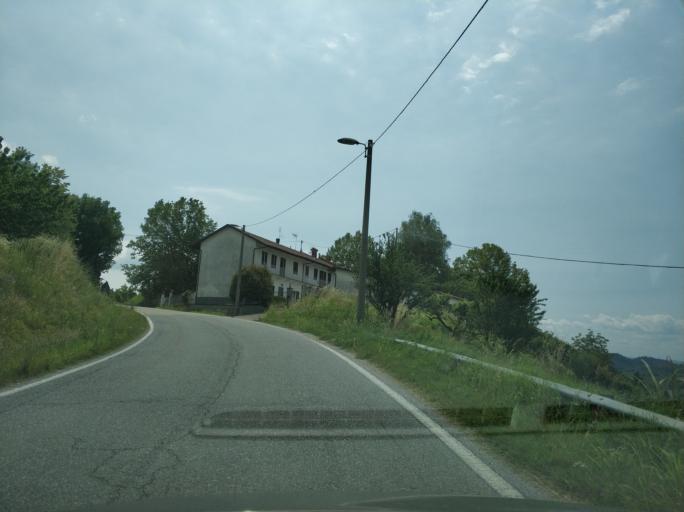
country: IT
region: Piedmont
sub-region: Provincia di Cuneo
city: Santo Stefano Roero
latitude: 44.7851
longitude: 7.9452
